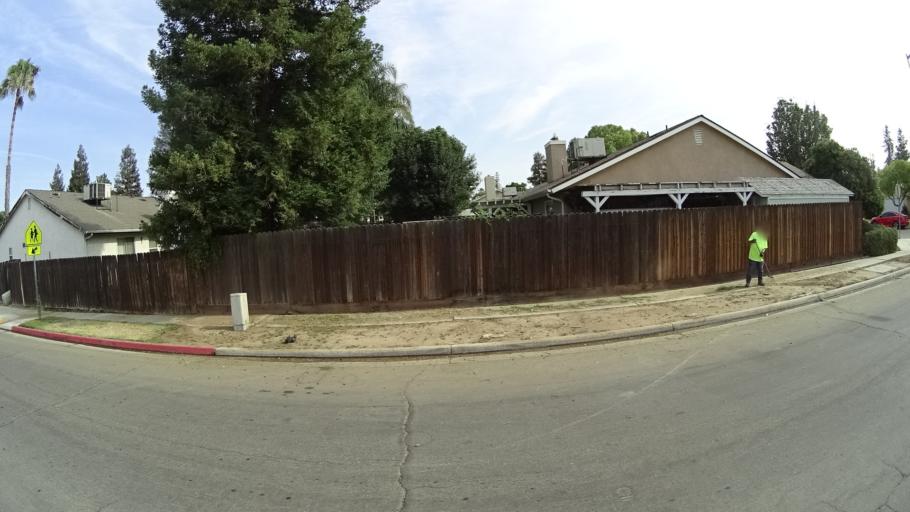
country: US
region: California
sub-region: Fresno County
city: West Park
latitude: 36.7682
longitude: -119.8732
